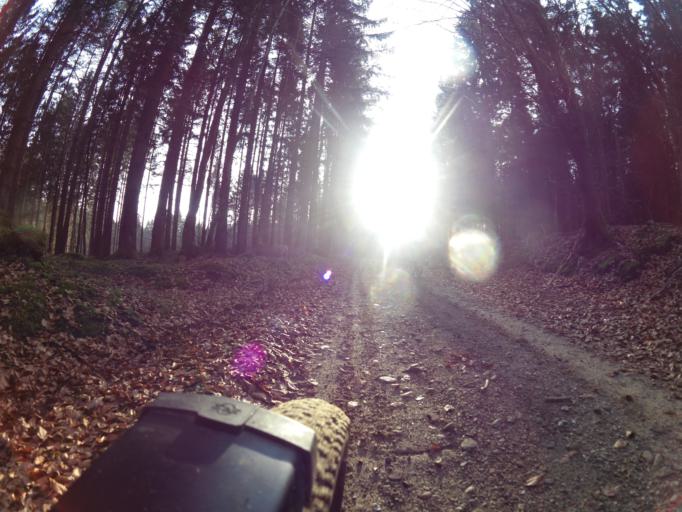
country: PL
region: West Pomeranian Voivodeship
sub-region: Powiat koszalinski
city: Polanow
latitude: 54.1713
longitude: 16.7275
